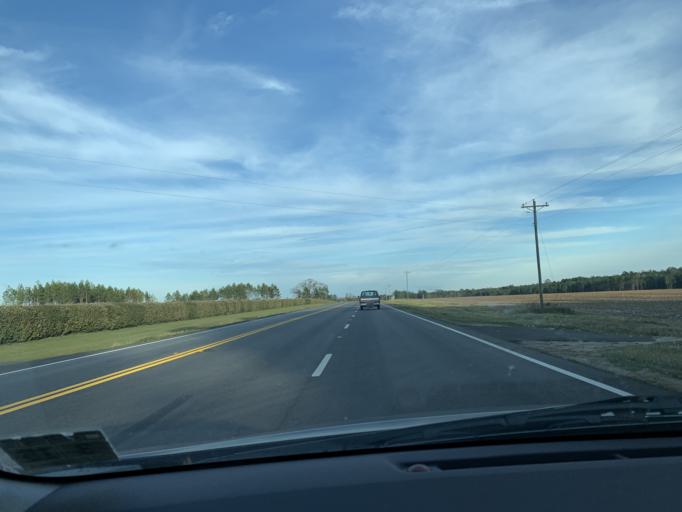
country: US
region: Georgia
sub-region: Irwin County
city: Ocilla
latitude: 31.5943
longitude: -83.1874
